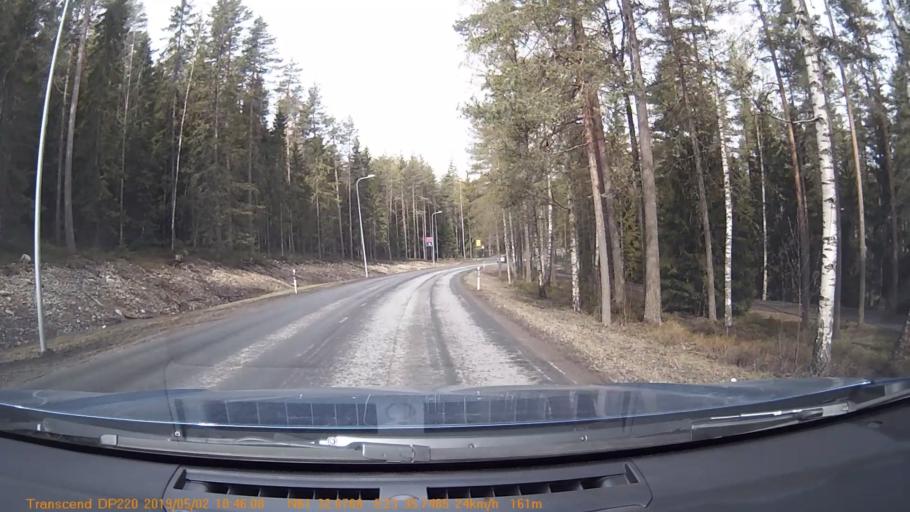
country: FI
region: Pirkanmaa
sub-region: Tampere
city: Yloejaervi
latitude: 61.5446
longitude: 23.5957
